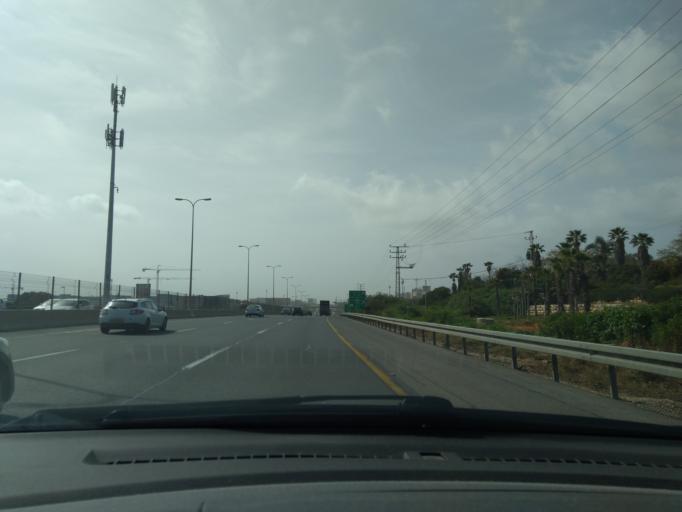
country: IL
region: Central District
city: Even Yehuda
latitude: 32.2960
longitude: 34.8621
